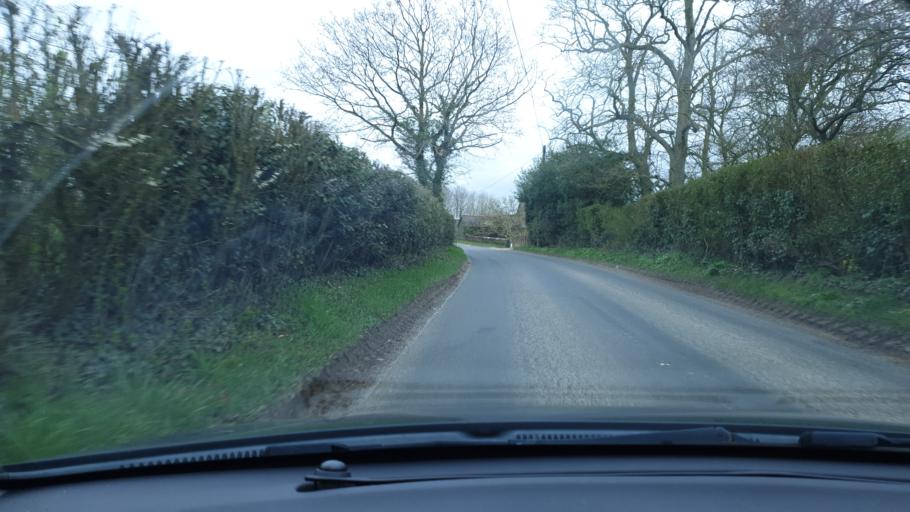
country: GB
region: England
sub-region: Essex
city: Mistley
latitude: 51.9067
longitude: 1.1192
